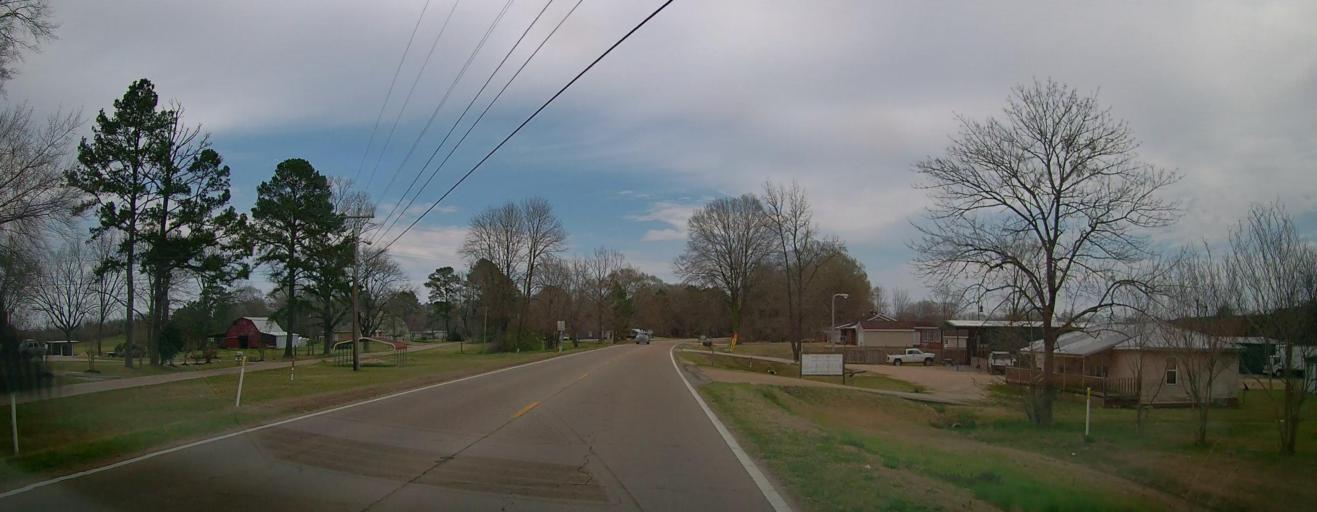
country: US
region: Mississippi
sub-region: Lee County
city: Plantersville
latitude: 34.2648
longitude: -88.6390
